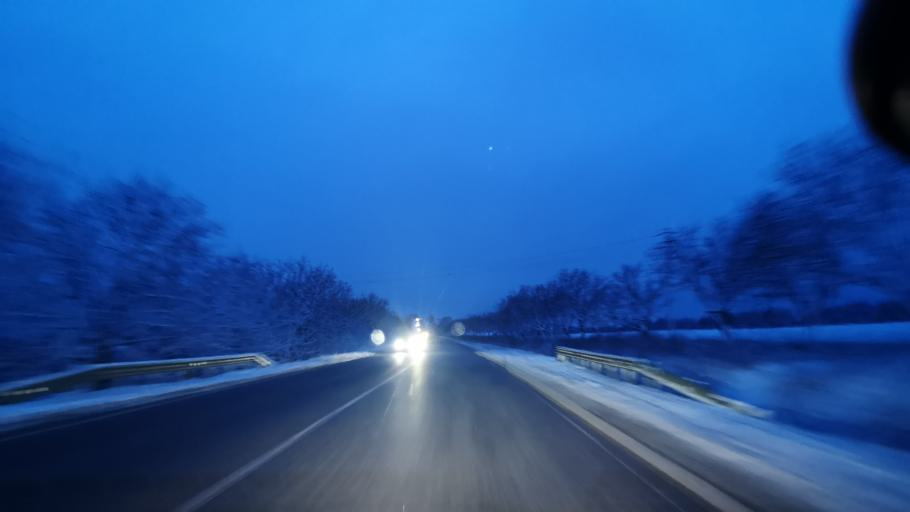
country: MD
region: Orhei
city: Orhei
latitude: 47.5470
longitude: 28.7927
